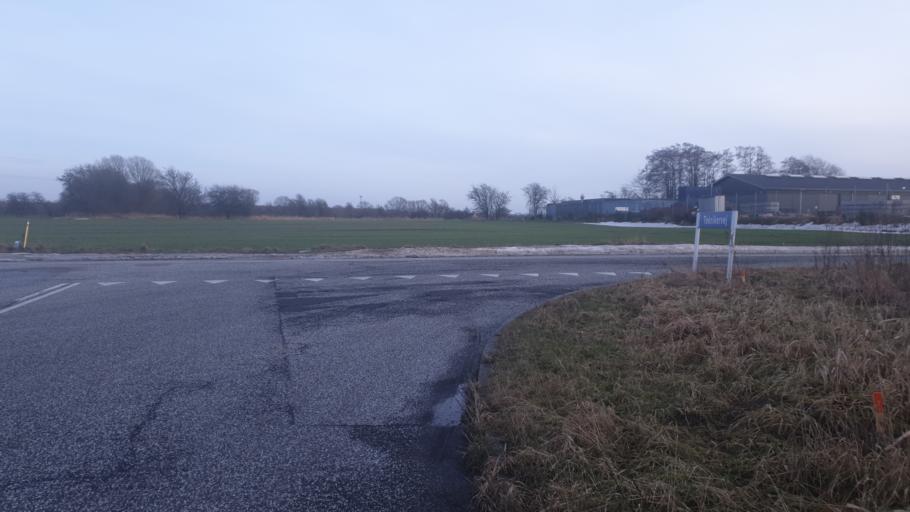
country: DK
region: Central Jutland
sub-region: Hedensted Kommune
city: Hedensted
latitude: 55.7877
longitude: 9.6839
